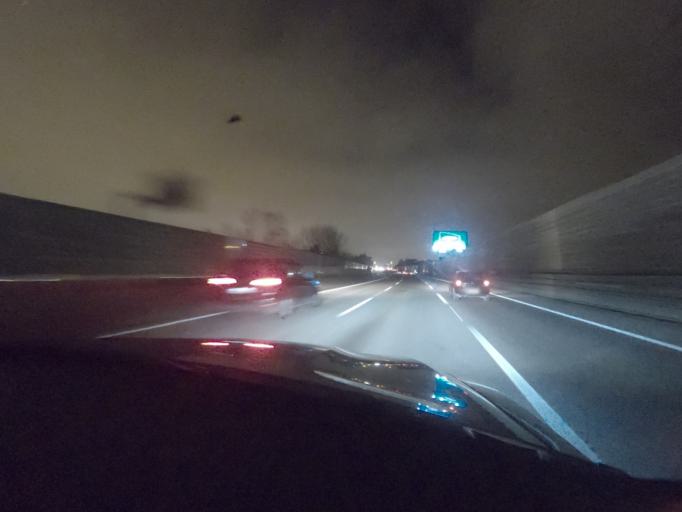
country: PT
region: Lisbon
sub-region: Vila Franca de Xira
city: Sobralinho
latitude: 38.9019
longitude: -9.0437
